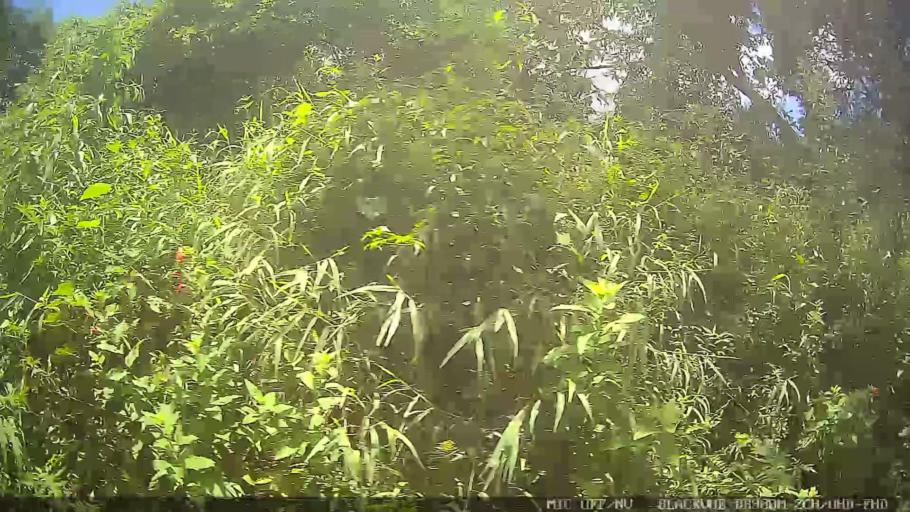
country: BR
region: Minas Gerais
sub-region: Extrema
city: Extrema
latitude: -22.8892
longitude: -46.3116
